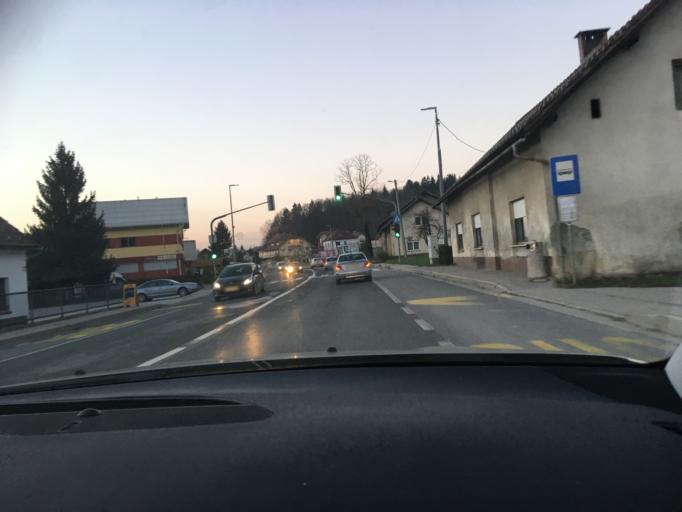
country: SI
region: Skofljica
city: Skofljica
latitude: 45.9894
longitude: 14.5666
